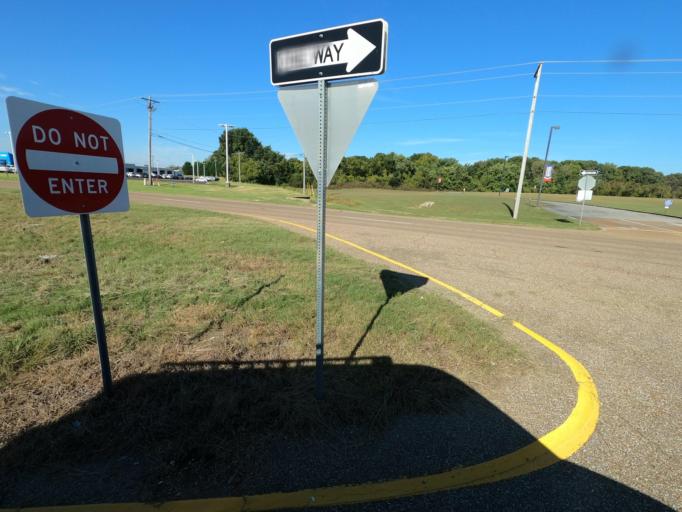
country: US
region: Tennessee
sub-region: Tipton County
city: Covington
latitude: 35.5285
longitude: -89.6855
